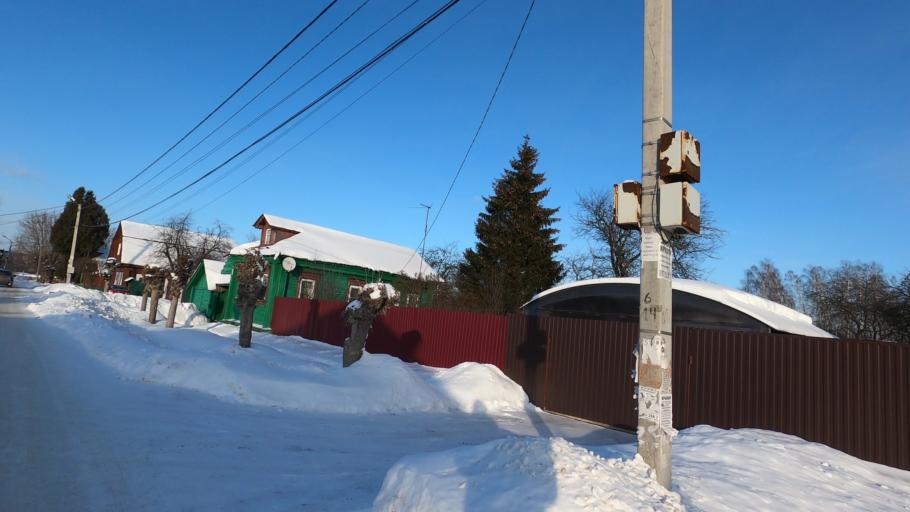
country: RU
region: Moskovskaya
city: Pavlovskiy Posad
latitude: 55.7715
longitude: 38.6977
